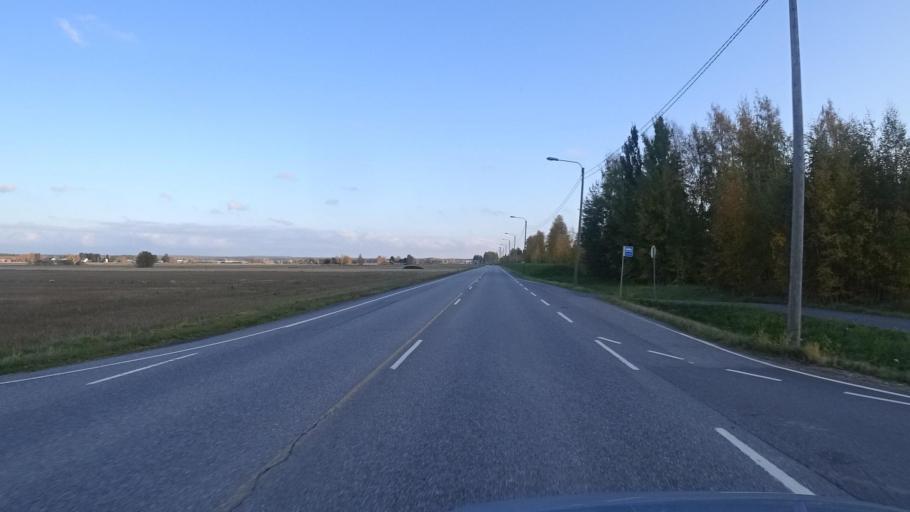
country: FI
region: Satakunta
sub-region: Rauma
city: Saekylae
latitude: 61.0543
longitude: 22.3352
